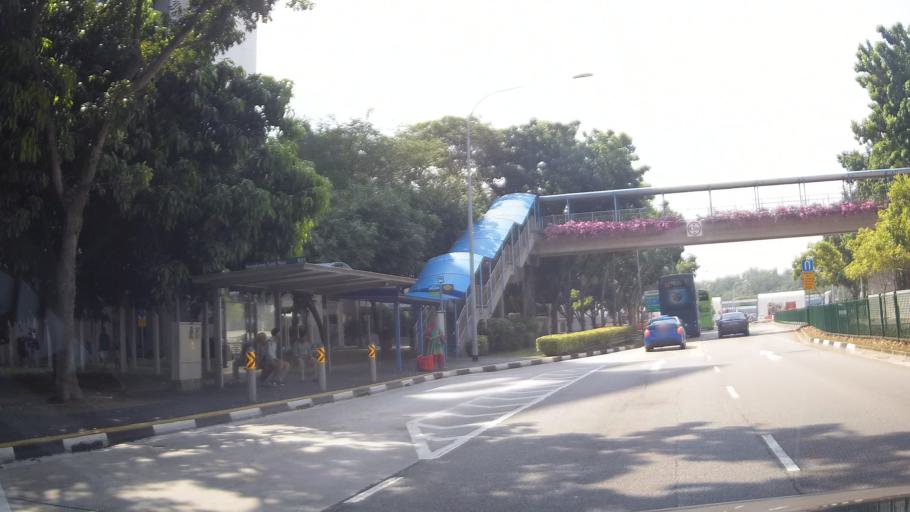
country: MY
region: Johor
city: Kampung Pasir Gudang Baru
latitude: 1.3880
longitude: 103.9066
